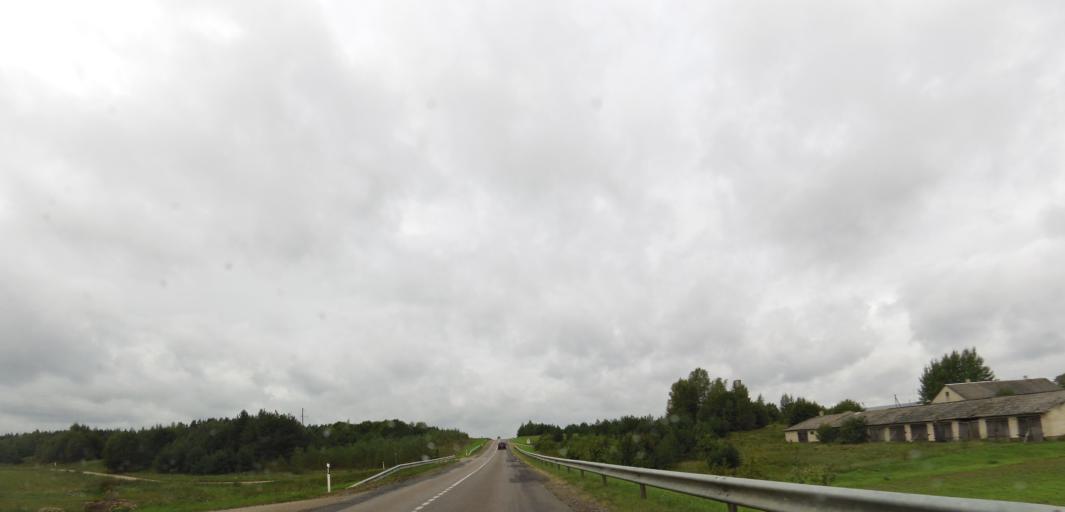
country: LT
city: Moletai
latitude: 55.2143
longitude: 25.2652
